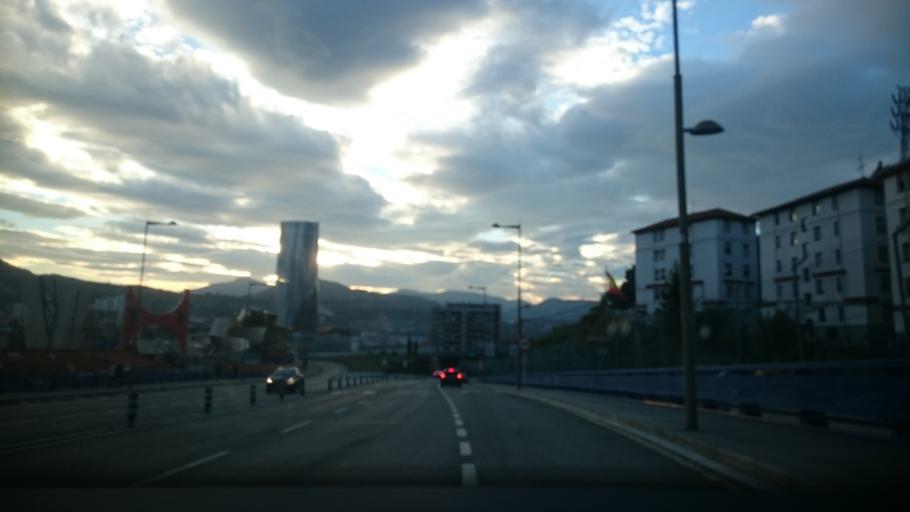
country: ES
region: Basque Country
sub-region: Bizkaia
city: Bilbao
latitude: 43.2705
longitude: -2.9284
